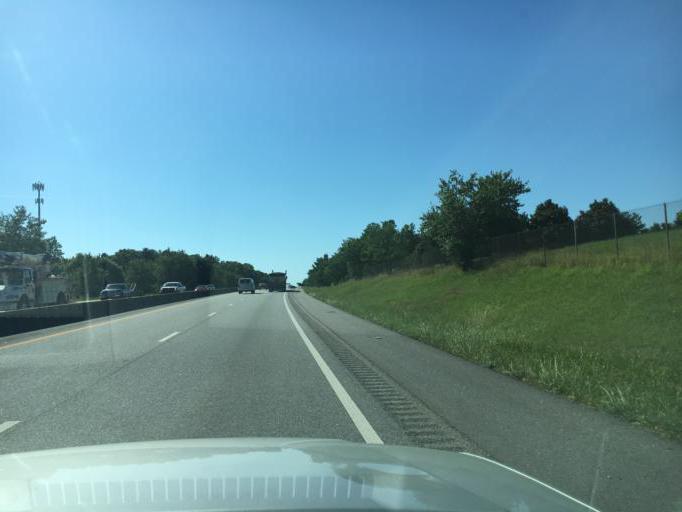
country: US
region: South Carolina
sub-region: Spartanburg County
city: Saxon
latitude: 34.9812
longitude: -81.9538
